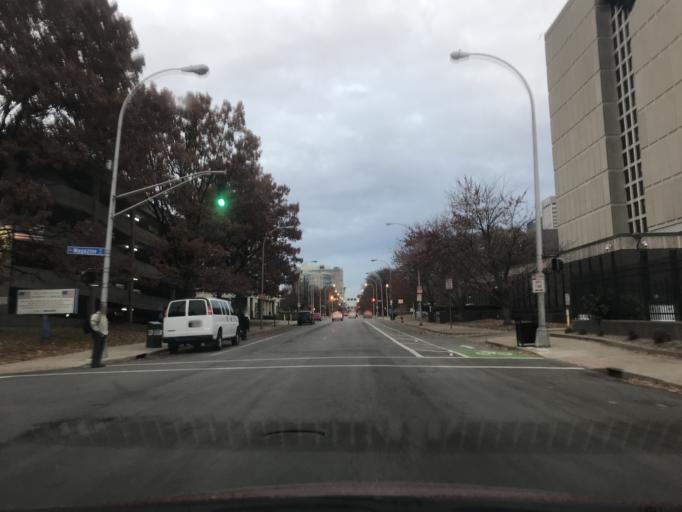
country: US
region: Kentucky
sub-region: Jefferson County
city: Louisville
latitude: 38.2481
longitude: -85.7631
